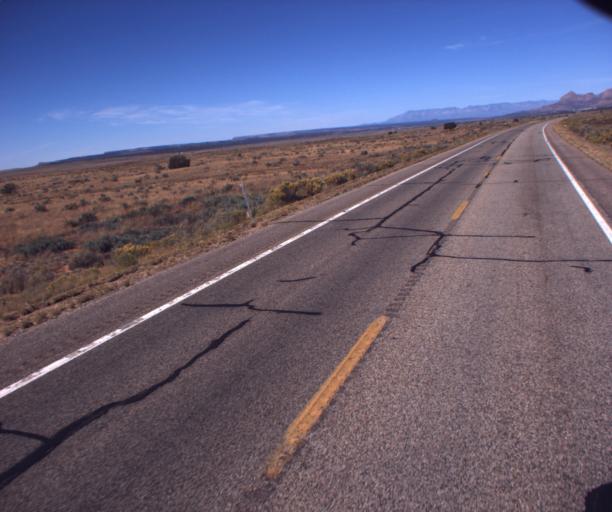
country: US
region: Arizona
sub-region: Mohave County
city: Colorado City
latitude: 36.8913
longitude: -112.9118
